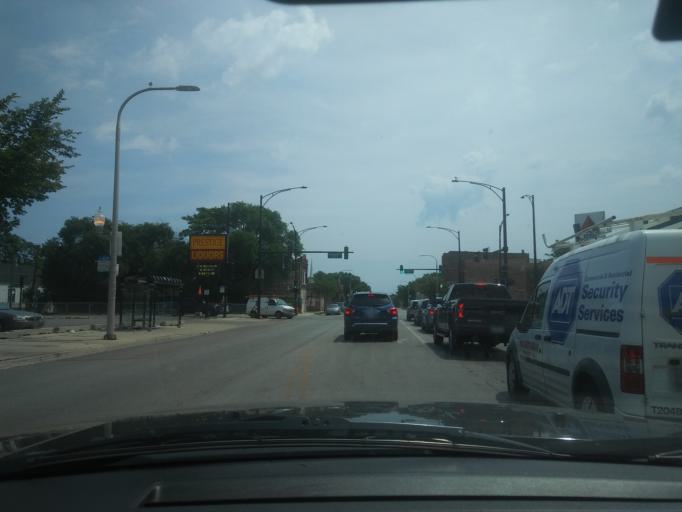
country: US
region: Illinois
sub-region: Cook County
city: Evergreen Park
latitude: 41.7792
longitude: -87.6744
